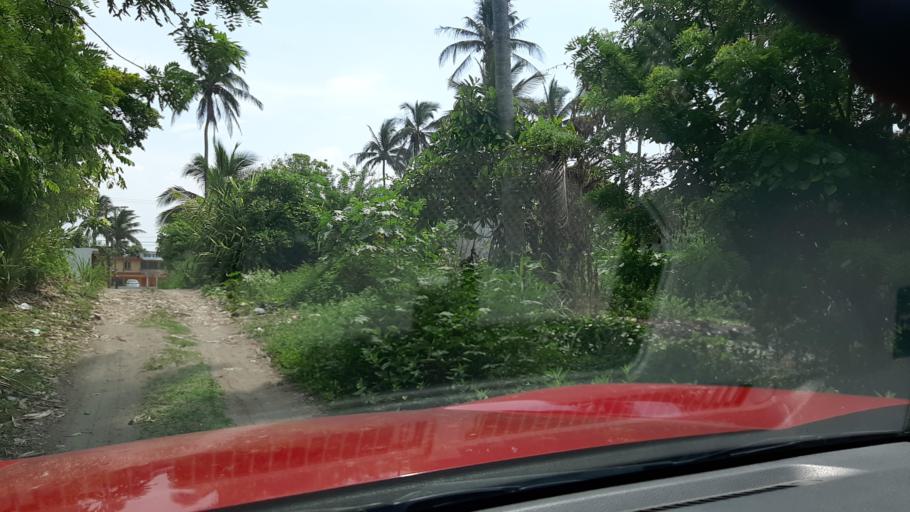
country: MX
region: Veracruz
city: Nautla
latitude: 20.2600
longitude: -96.8026
